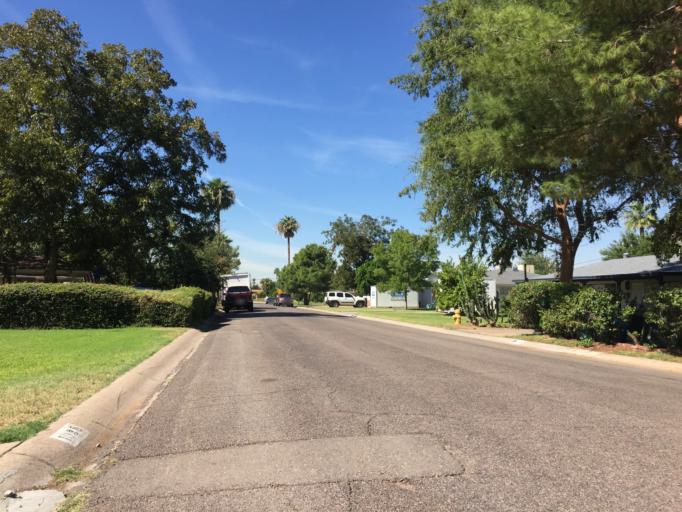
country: US
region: Arizona
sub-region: Maricopa County
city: Phoenix
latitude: 33.5337
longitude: -112.0591
